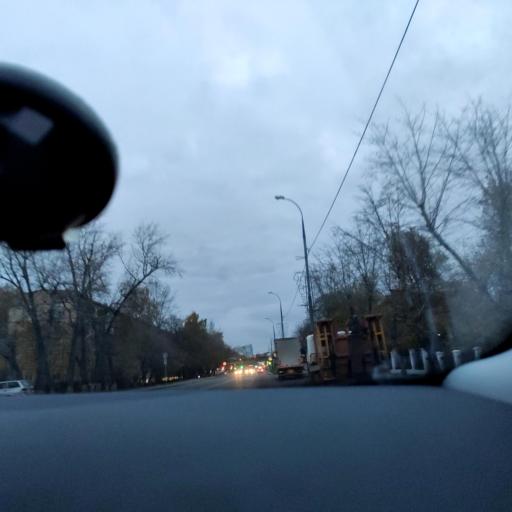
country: RU
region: Moscow
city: Kuz'minki
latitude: 55.6993
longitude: 37.7921
